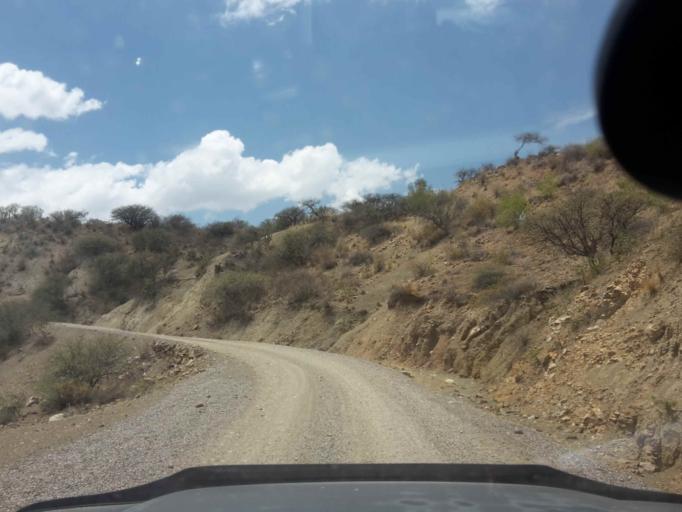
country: BO
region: Cochabamba
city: Sipe Sipe
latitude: -17.5468
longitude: -66.4791
